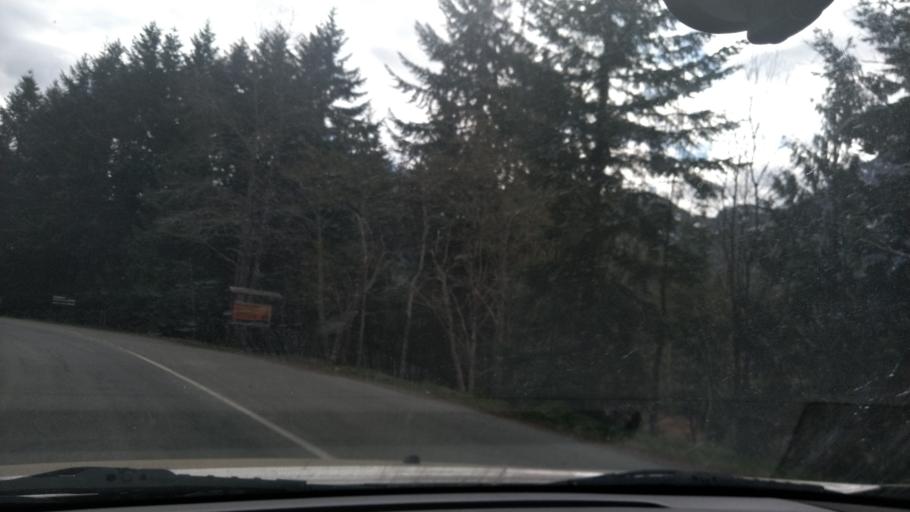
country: CA
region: British Columbia
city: Campbell River
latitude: 49.8374
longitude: -125.6306
